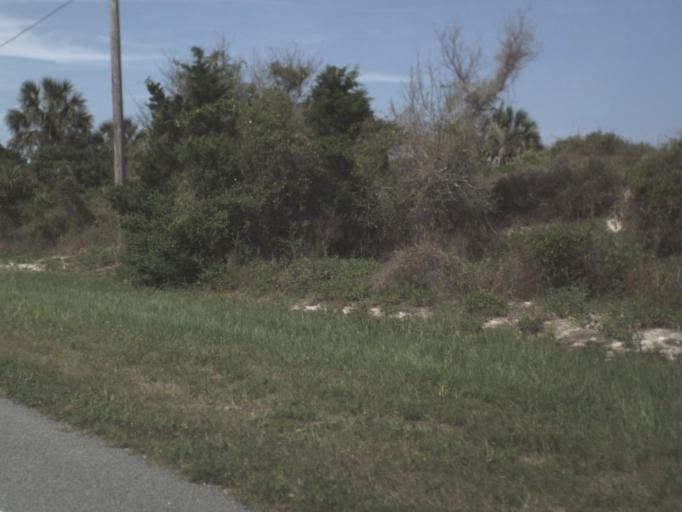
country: US
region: Florida
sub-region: Duval County
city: Atlantic Beach
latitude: 30.4441
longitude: -81.4156
